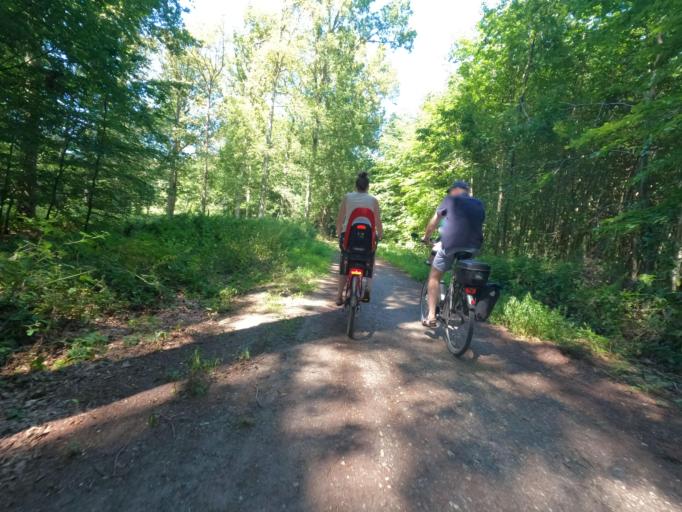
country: DE
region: North Rhine-Westphalia
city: Wegberg
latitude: 51.1442
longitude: 6.3068
